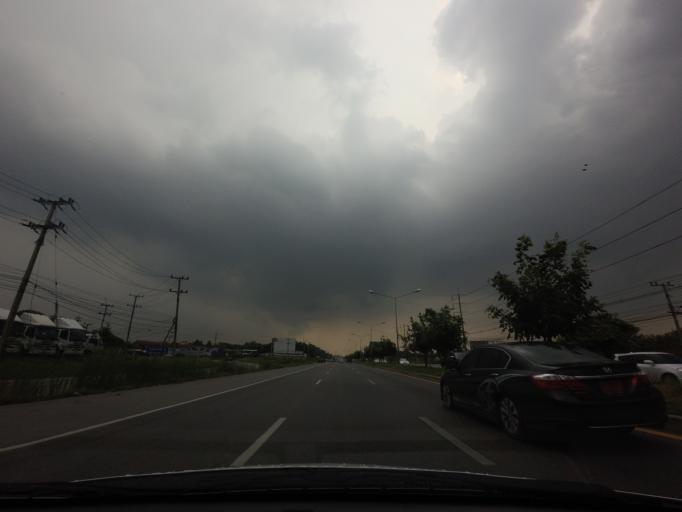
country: TH
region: Nakhon Pathom
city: Sam Phran
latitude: 13.7837
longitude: 100.2485
